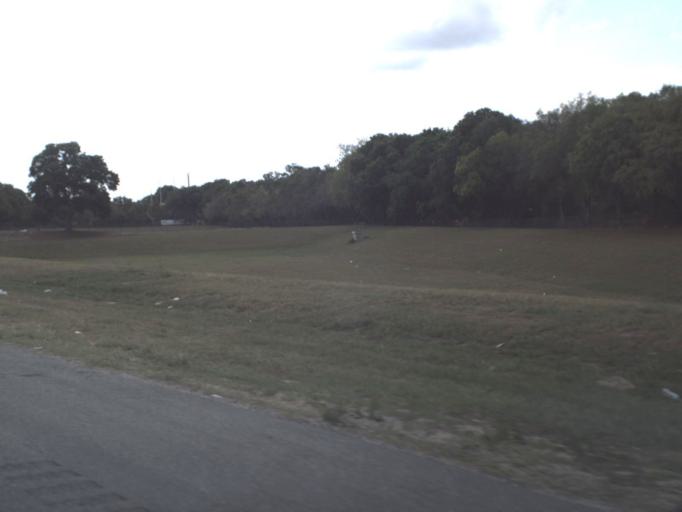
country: US
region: Florida
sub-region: Orange County
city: Paradise Heights
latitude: 28.6272
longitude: -81.5376
